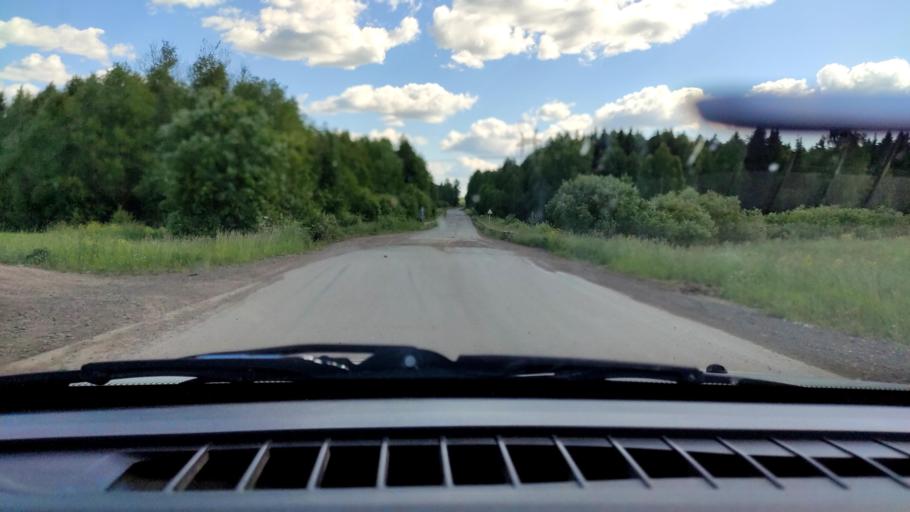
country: RU
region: Perm
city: Uinskoye
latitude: 57.1552
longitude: 56.5718
